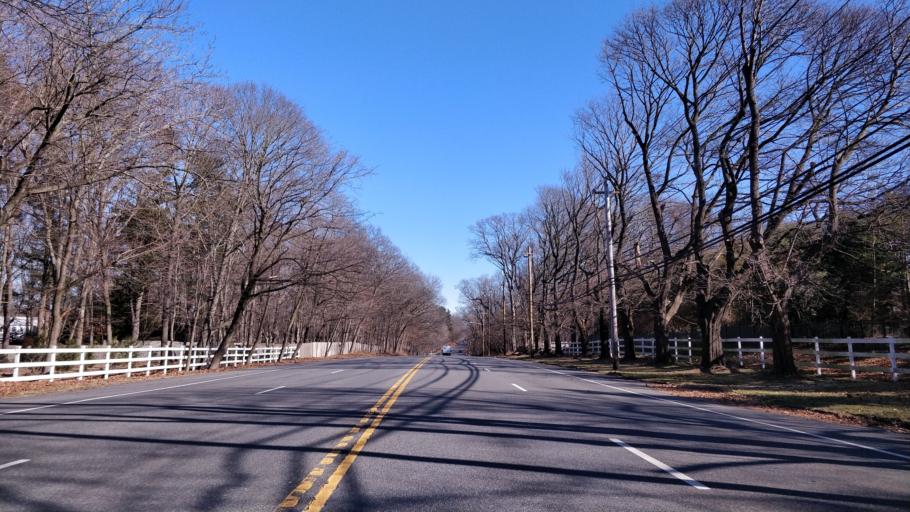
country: US
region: New York
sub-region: Nassau County
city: Upper Brookville
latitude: 40.8360
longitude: -73.5602
